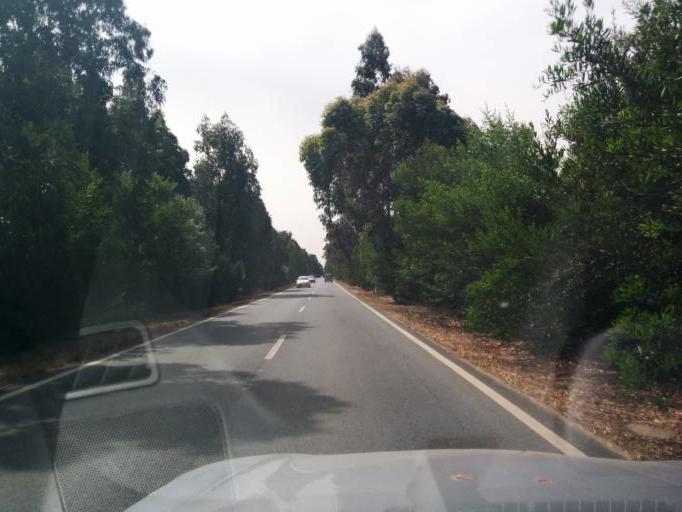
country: PT
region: Beja
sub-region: Odemira
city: Vila Nova de Milfontes
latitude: 37.6839
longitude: -8.7643
